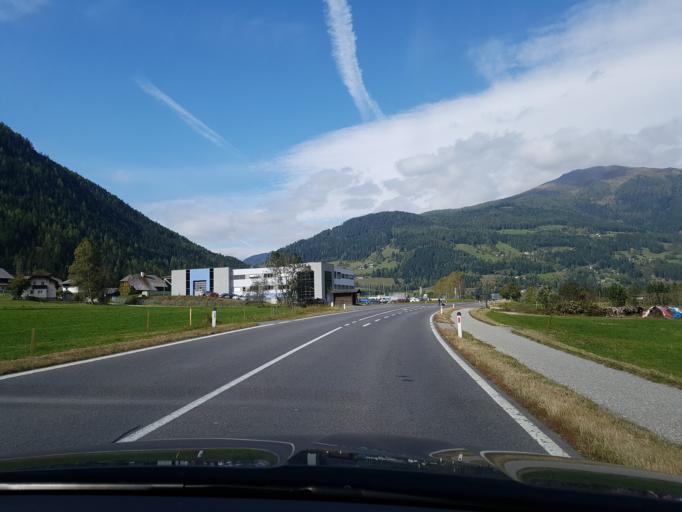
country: AT
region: Carinthia
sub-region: Politischer Bezirk Villach Land
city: Arriach
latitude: 46.8093
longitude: 13.8738
